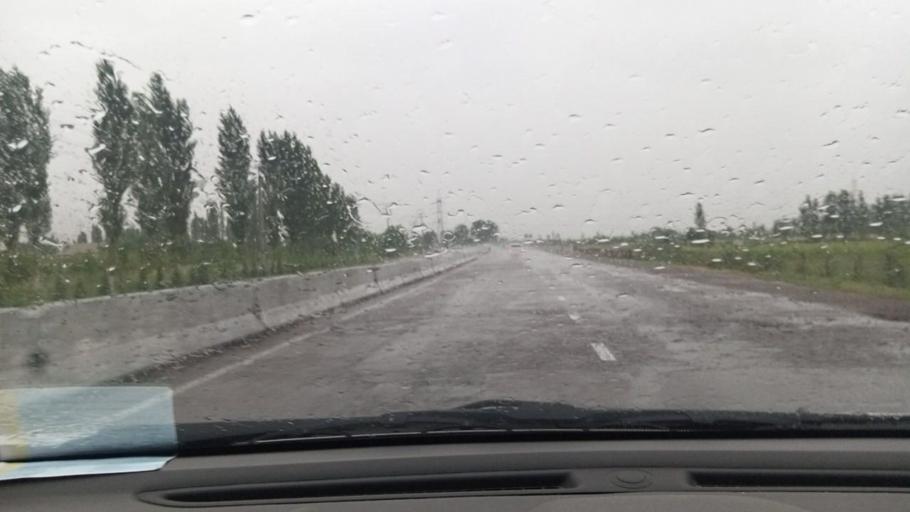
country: UZ
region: Toshkent
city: Ohangaron
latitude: 40.9147
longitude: 69.8260
